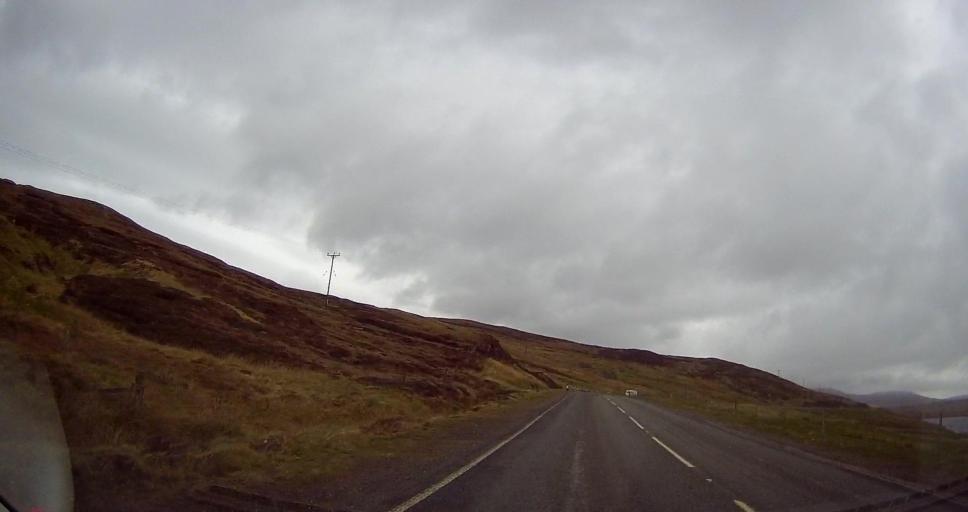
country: GB
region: Scotland
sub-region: Shetland Islands
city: Lerwick
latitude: 60.2532
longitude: -1.2260
